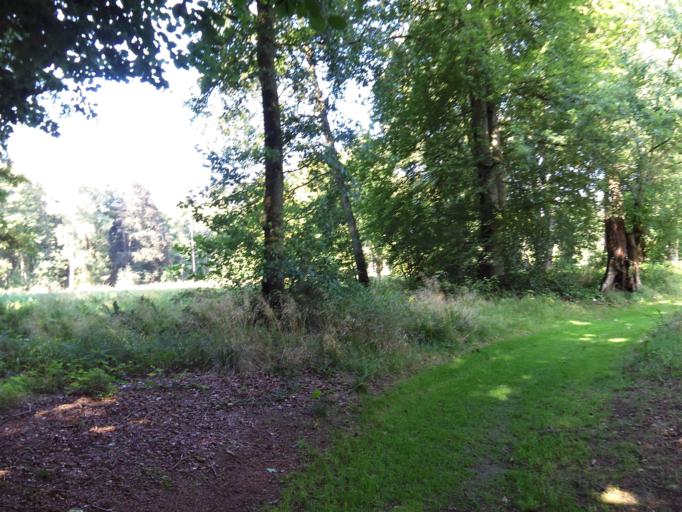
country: DE
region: Lower Saxony
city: Soltau
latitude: 52.9759
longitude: 9.8419
